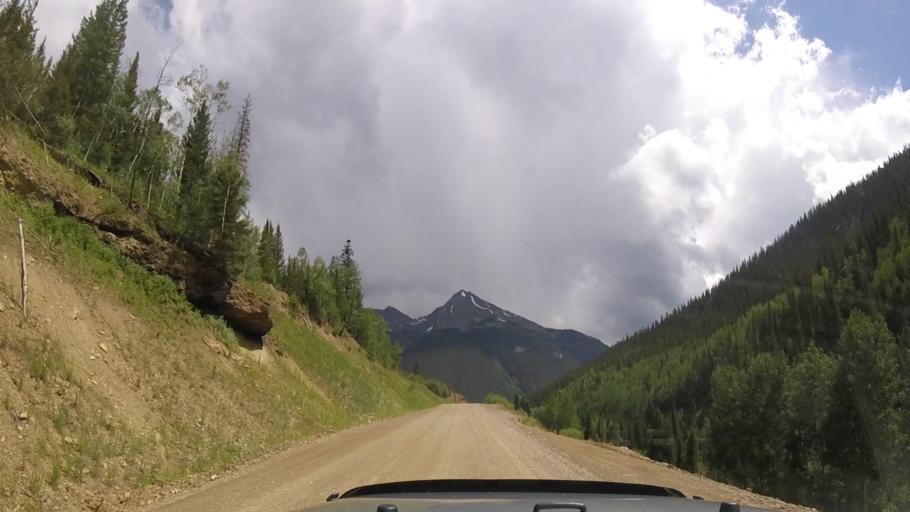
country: US
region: Colorado
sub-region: San Juan County
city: Silverton
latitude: 37.8244
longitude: -107.6664
